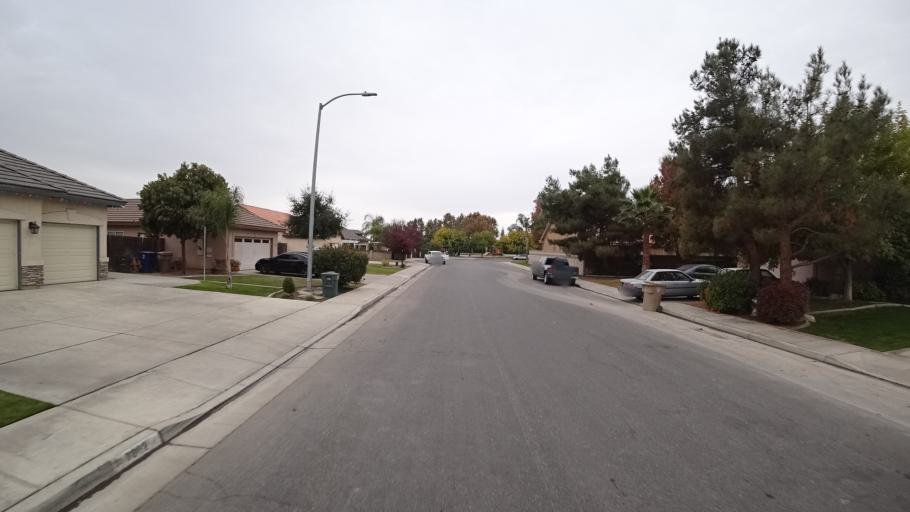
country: US
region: California
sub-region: Kern County
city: Greenfield
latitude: 35.2842
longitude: -119.0306
